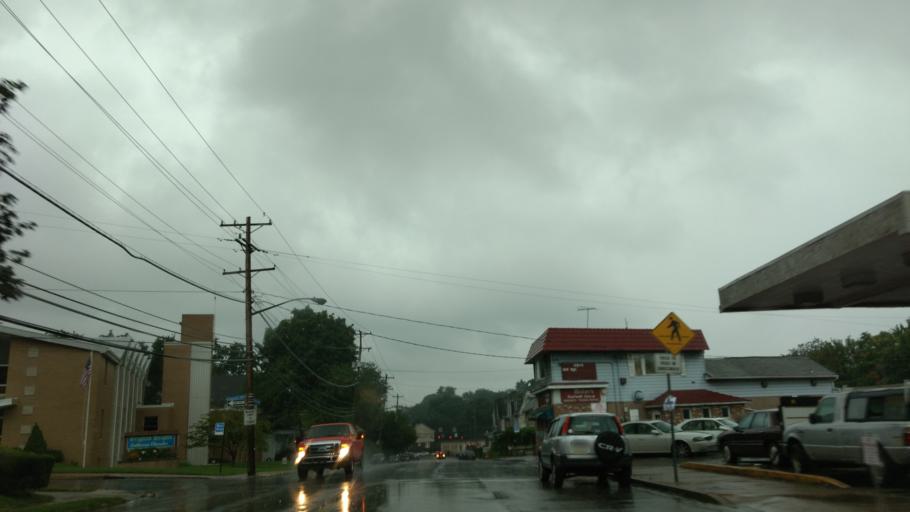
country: US
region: Pennsylvania
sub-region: Allegheny County
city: Bellevue
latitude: 40.4856
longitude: -80.0423
